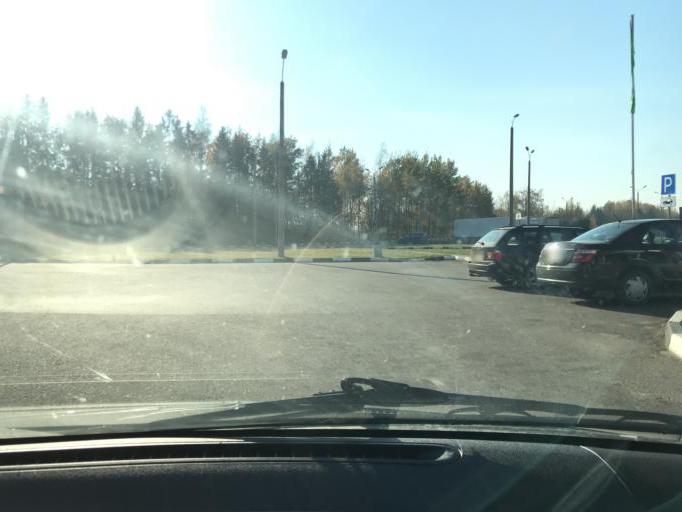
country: BY
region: Mogilev
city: Shklow
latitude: 54.2193
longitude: 30.4507
